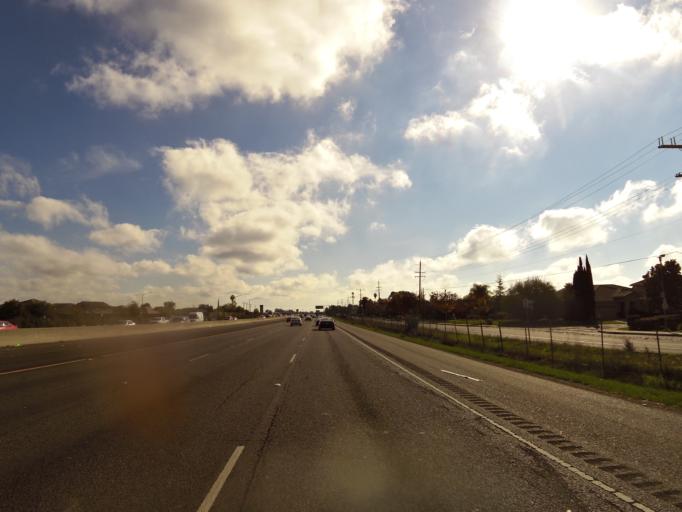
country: US
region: California
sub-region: Sacramento County
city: Laguna
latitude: 38.4461
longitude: -121.4055
